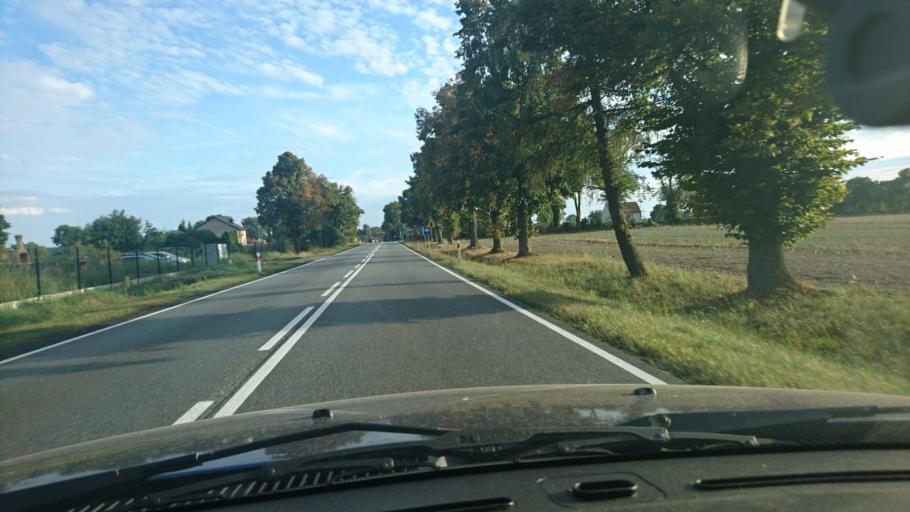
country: PL
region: Opole Voivodeship
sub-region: Powiat kluczborski
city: Kluczbork
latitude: 51.0317
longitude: 18.1927
